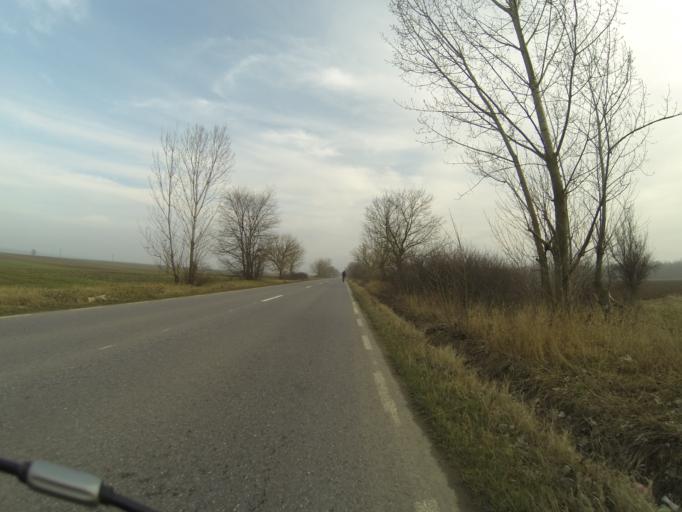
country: RO
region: Mehedinti
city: Vanju-Mare
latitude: 44.4058
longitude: 22.8951
